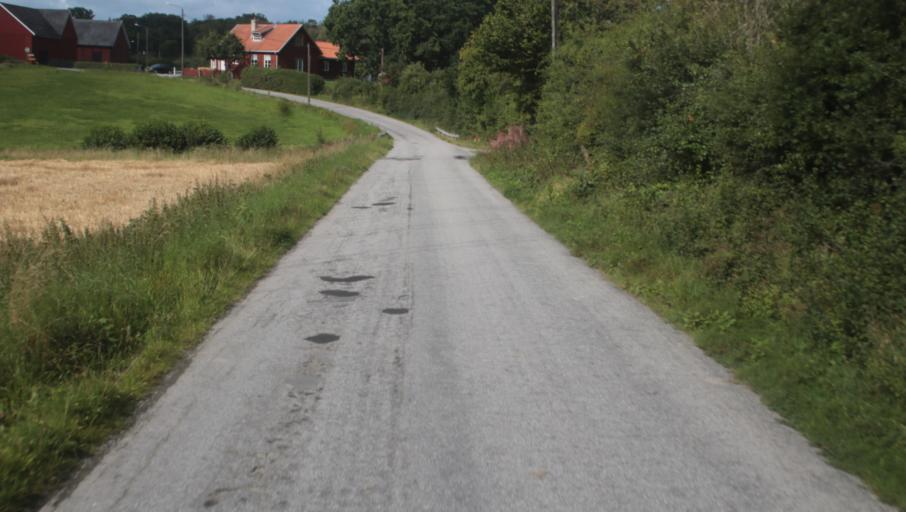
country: SE
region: Blekinge
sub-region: Karlshamns Kommun
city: Karlshamn
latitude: 56.1837
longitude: 14.8196
